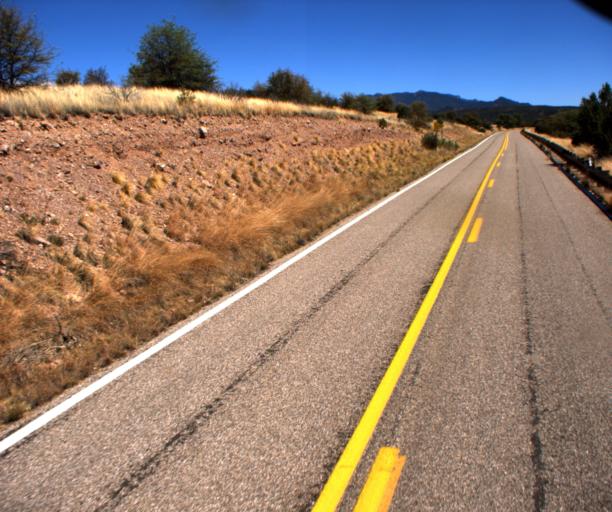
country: US
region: Arizona
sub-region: Cochise County
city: Sierra Vista
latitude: 31.4901
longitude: -110.4886
